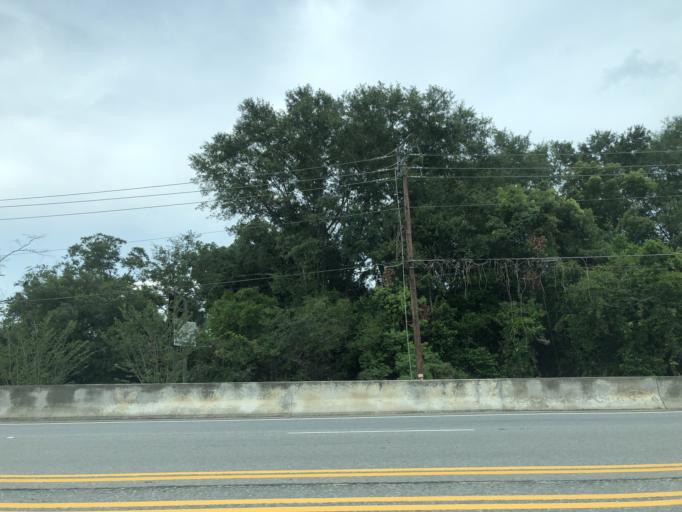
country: US
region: Georgia
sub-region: Wayne County
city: Jesup
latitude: 31.6060
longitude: -81.8792
